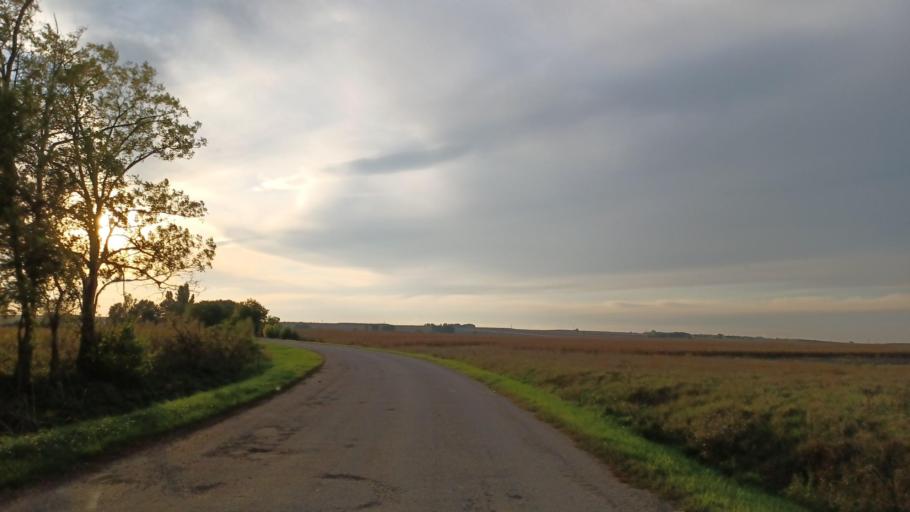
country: HU
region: Tolna
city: Dunafoldvar
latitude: 46.7943
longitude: 18.8880
